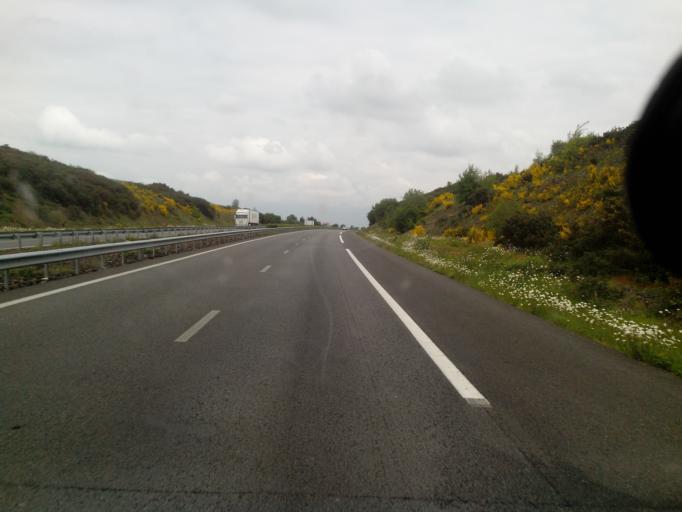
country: FR
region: Brittany
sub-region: Departement d'Ille-et-Vilaine
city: Saint-Jean-sur-Couesnon
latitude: 48.3078
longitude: -1.3539
